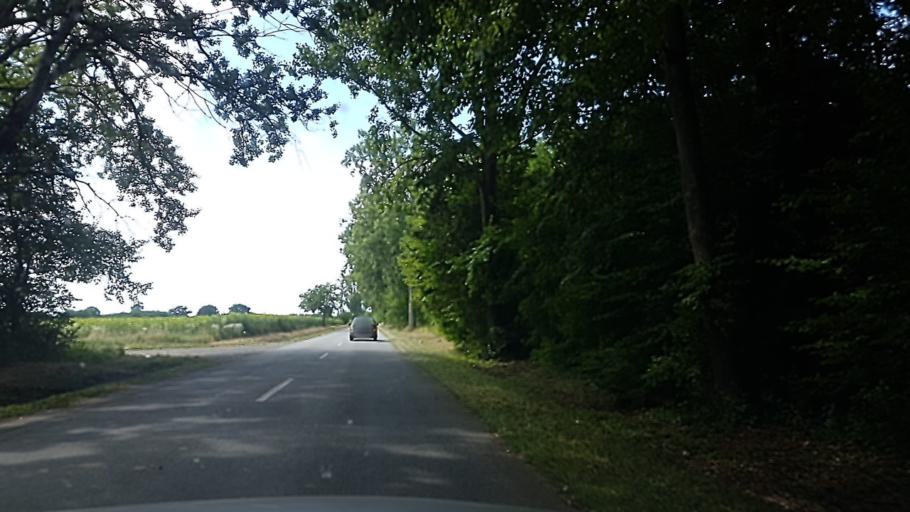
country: HU
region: Somogy
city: Barcs
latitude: 45.9485
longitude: 17.6275
